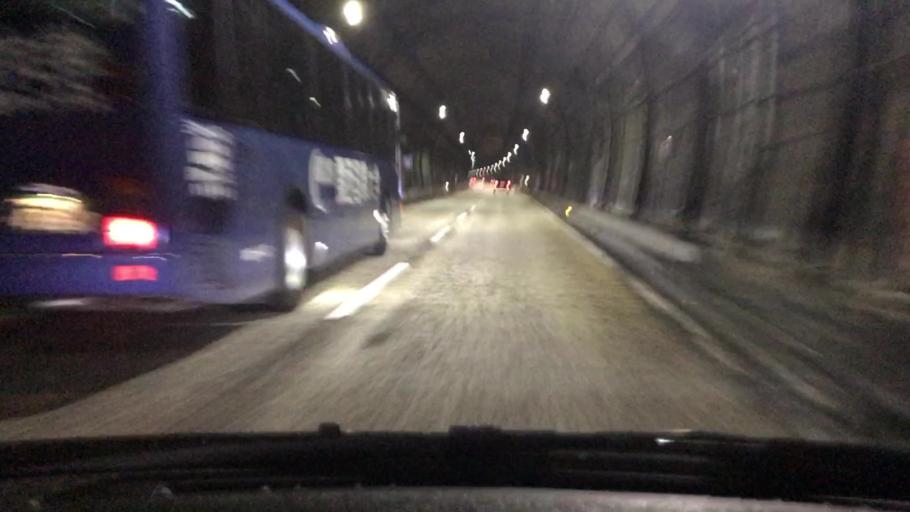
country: JP
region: Hyogo
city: Kobe
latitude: 34.7199
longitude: 135.1864
